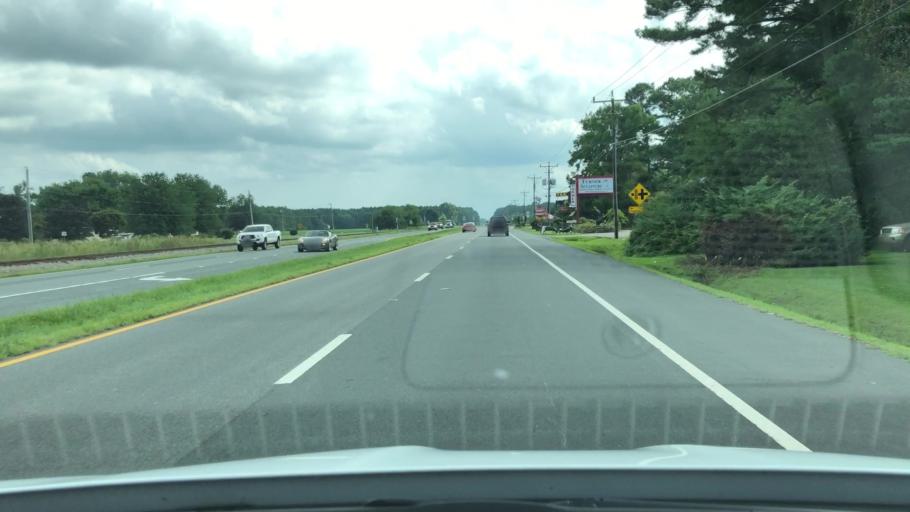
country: US
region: Virginia
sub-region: Accomack County
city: Onancock
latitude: 37.6675
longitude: -75.7310
